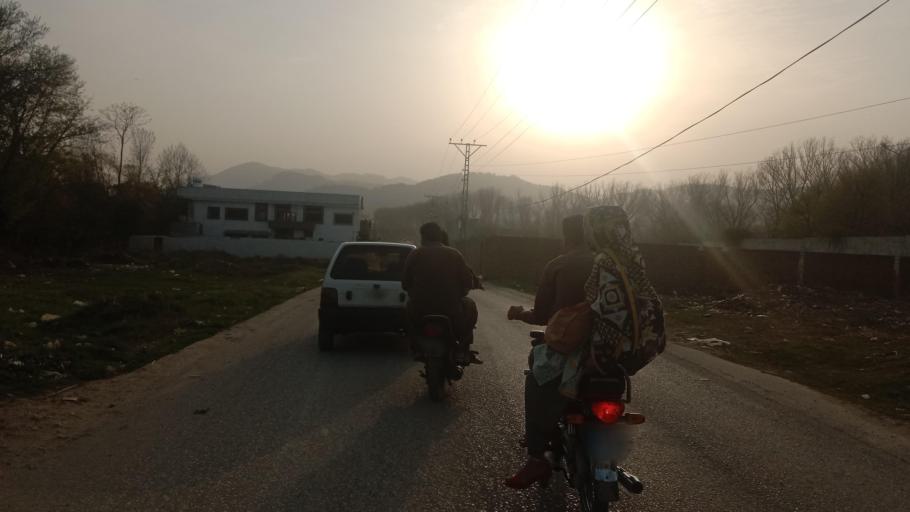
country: PK
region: Khyber Pakhtunkhwa
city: Abbottabad
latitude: 34.1749
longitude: 73.2427
